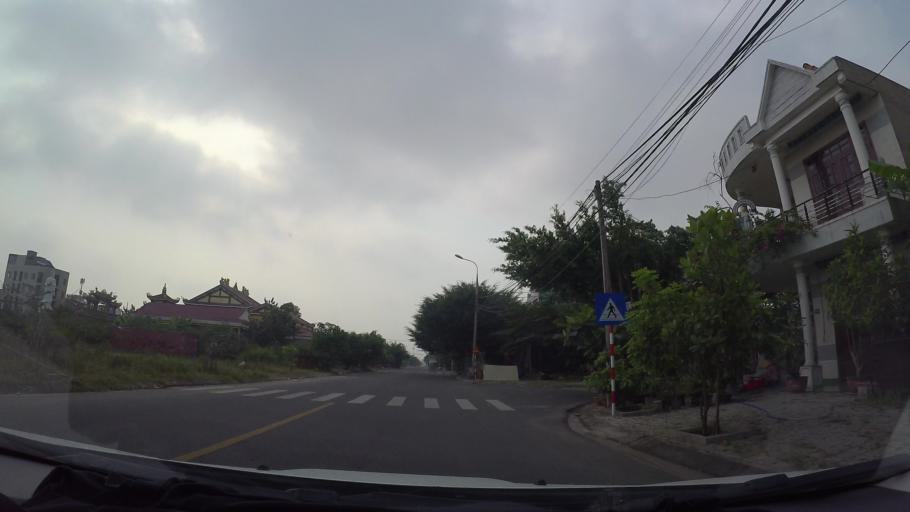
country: VN
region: Da Nang
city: Cam Le
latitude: 16.0059
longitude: 108.2180
